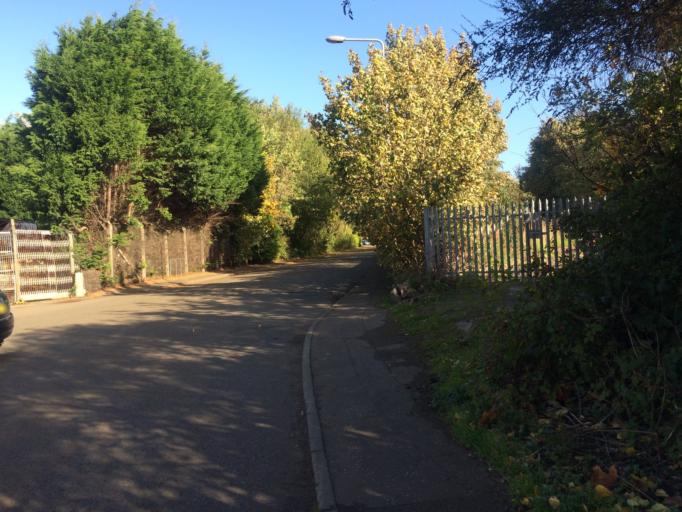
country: GB
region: Scotland
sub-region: Fife
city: Kirkcaldy
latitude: 56.1204
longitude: -3.1544
